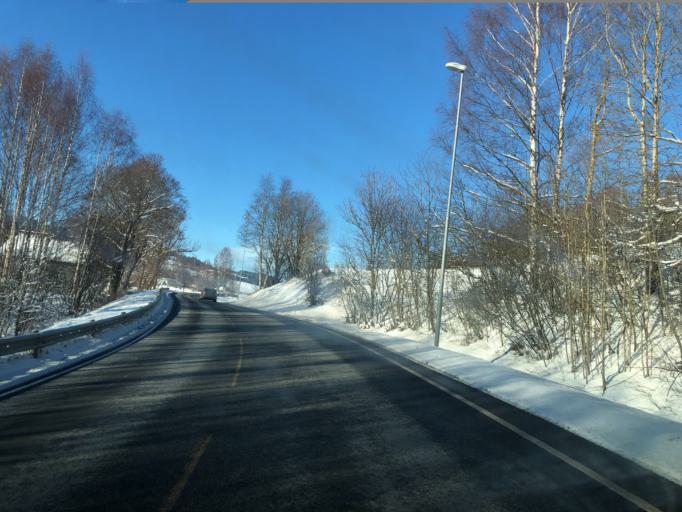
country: NO
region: Oppland
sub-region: Lunner
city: Roa
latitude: 60.3152
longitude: 10.5903
